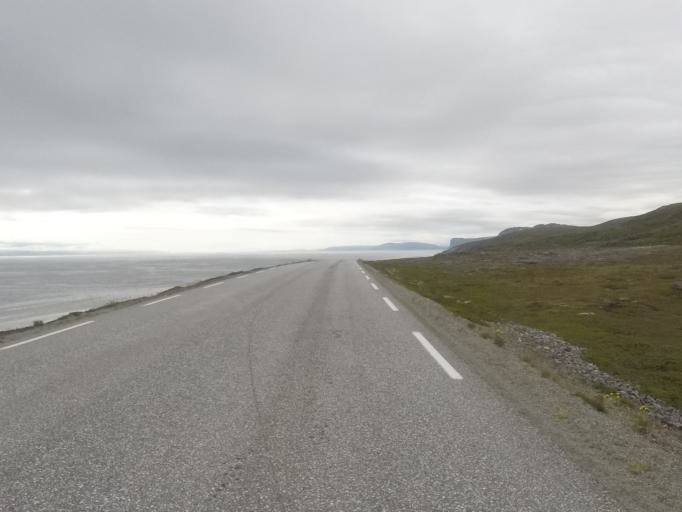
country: NO
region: Finnmark Fylke
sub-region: Nordkapp
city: Honningsvag
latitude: 70.7337
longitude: 25.6150
